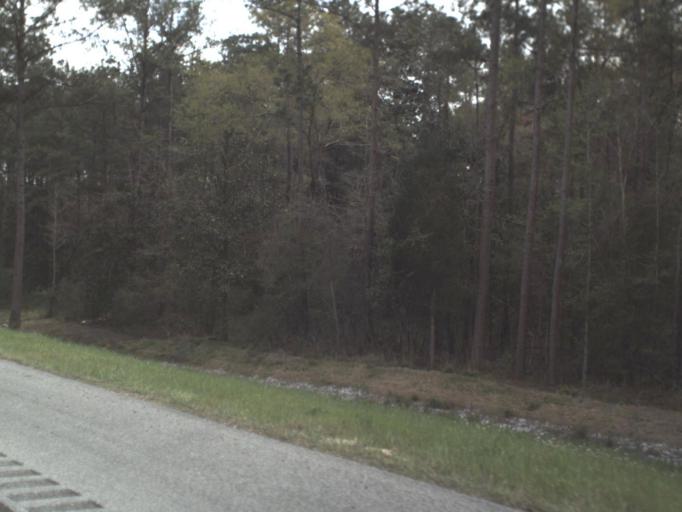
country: US
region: Florida
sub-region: Walton County
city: DeFuniak Springs
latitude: 30.6974
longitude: -86.1514
